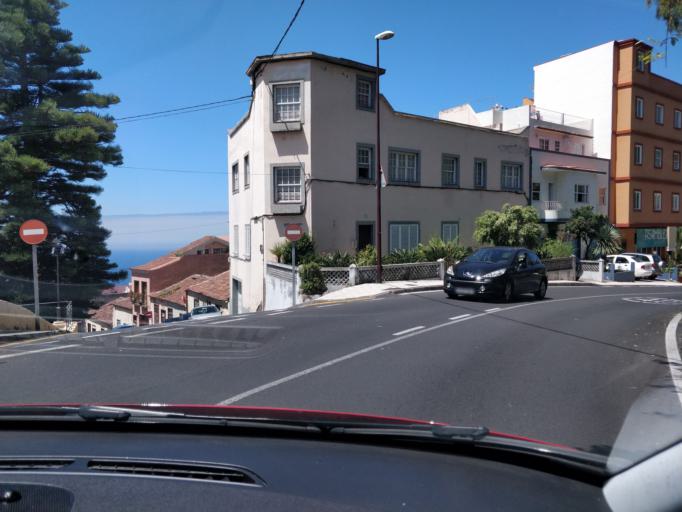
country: ES
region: Canary Islands
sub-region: Provincia de Santa Cruz de Tenerife
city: La Orotava
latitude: 28.3868
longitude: -16.5228
